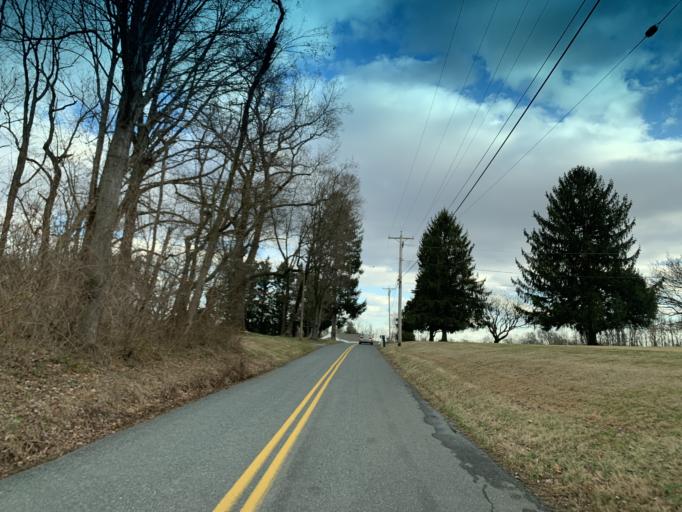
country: US
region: Maryland
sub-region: Harford County
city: South Bel Air
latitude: 39.6048
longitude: -76.3029
